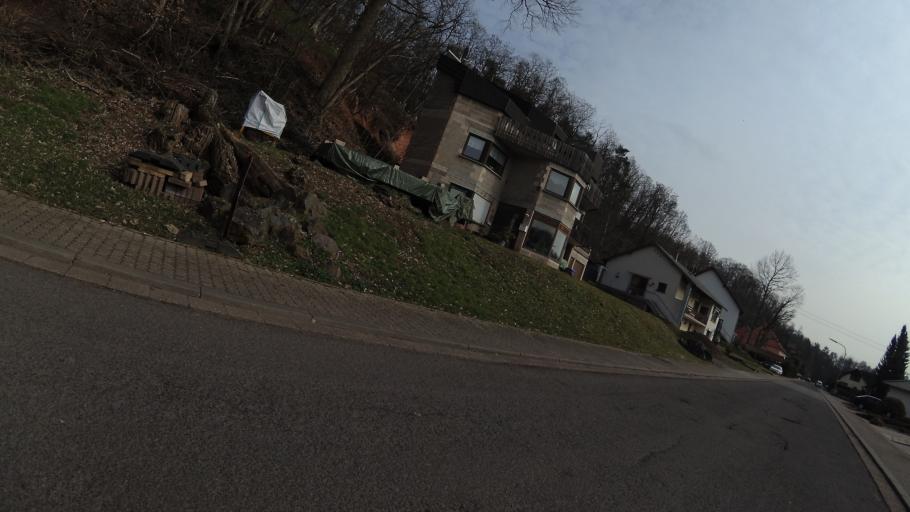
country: DE
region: Saarland
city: Nalbach
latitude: 49.4442
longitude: 6.7722
